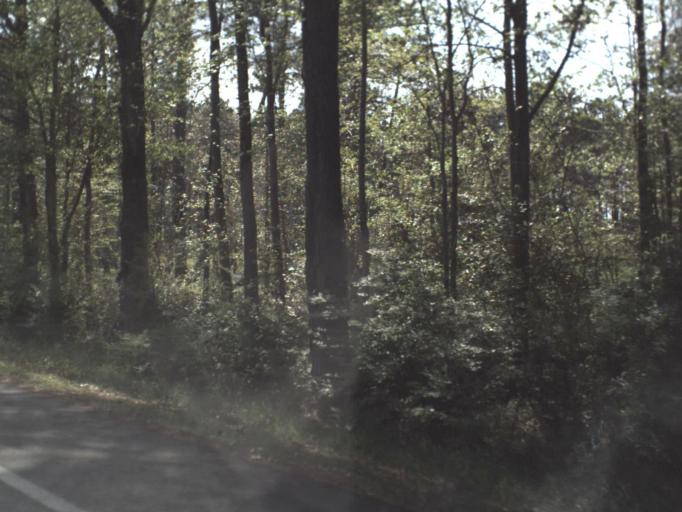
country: US
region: Alabama
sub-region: Covington County
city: Florala
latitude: 30.9549
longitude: -86.4714
